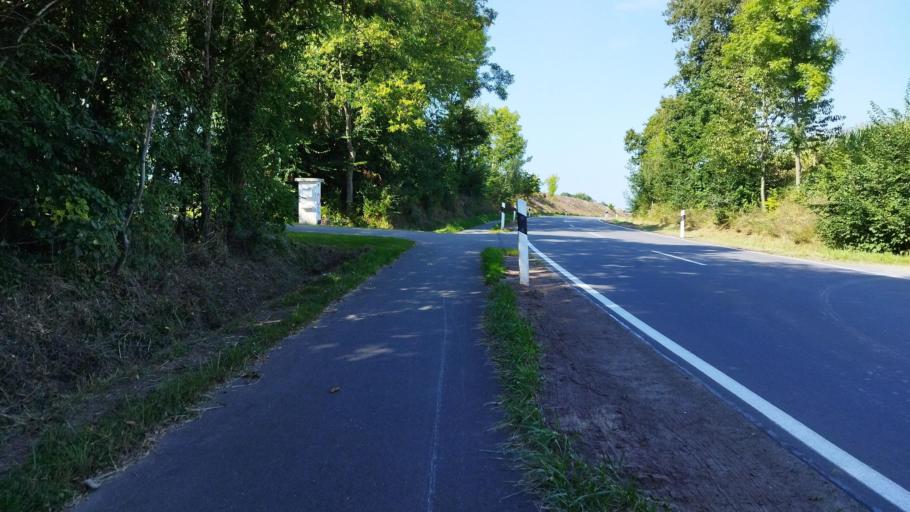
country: DE
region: Lower Saxony
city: Hasbergen
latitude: 52.2468
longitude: 7.9402
